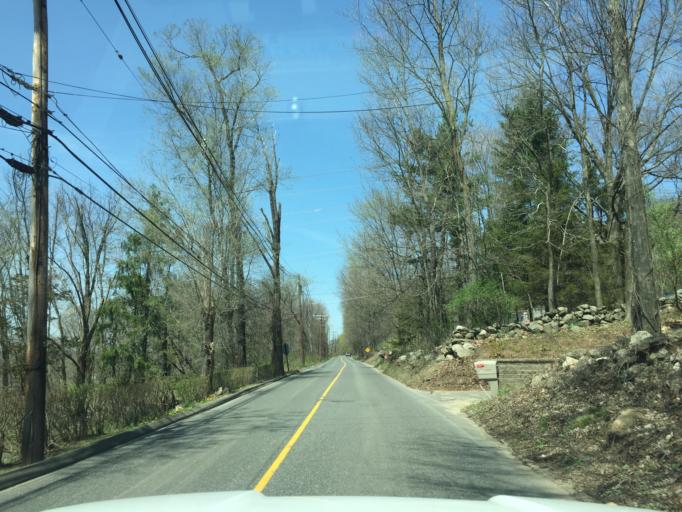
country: US
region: Connecticut
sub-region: Fairfield County
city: Bethel
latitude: 41.4069
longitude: -73.4024
